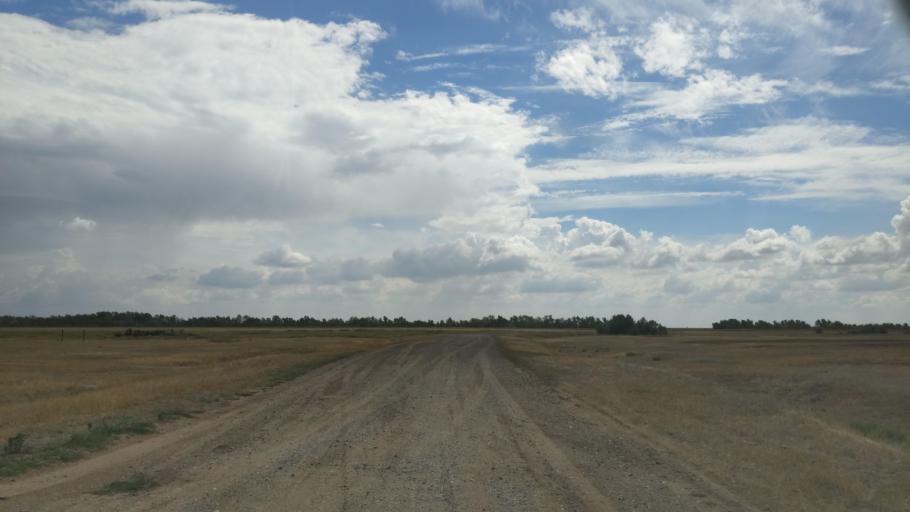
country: KZ
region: Pavlodar
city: Pavlodar
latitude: 52.6473
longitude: 77.0249
